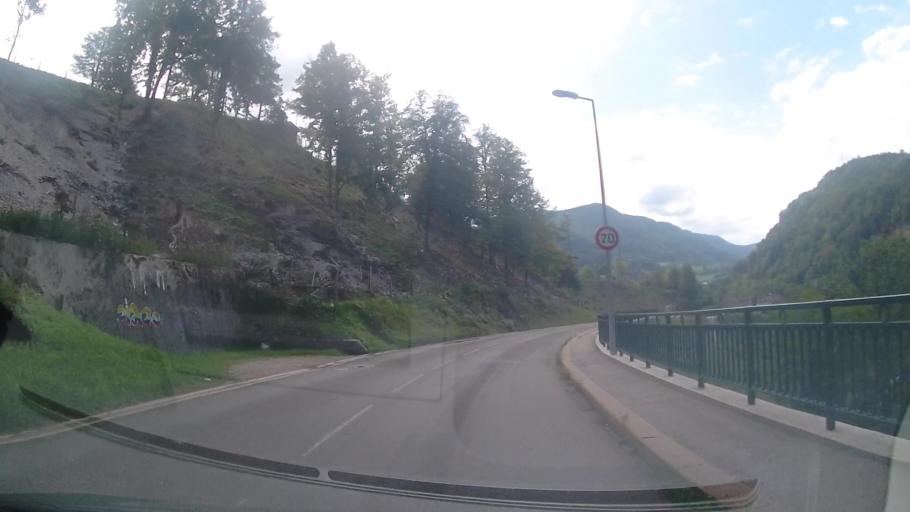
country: FR
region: Franche-Comte
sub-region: Departement du Jura
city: Saint-Claude
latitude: 46.3798
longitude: 5.8765
